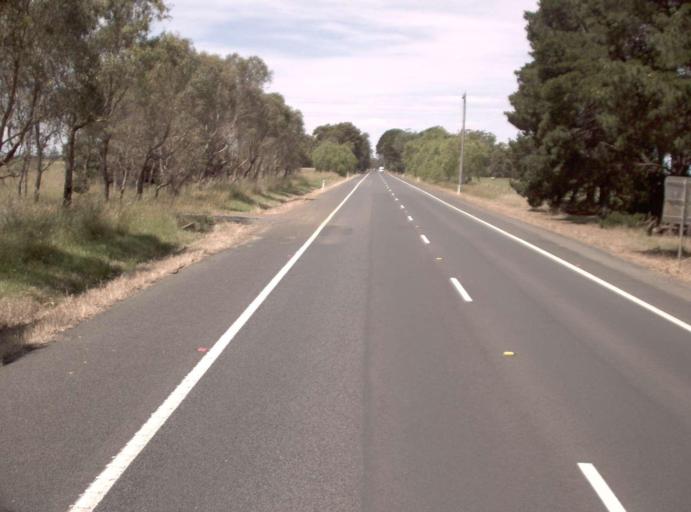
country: AU
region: Victoria
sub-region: Wellington
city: Heyfield
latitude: -38.1129
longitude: 146.8803
